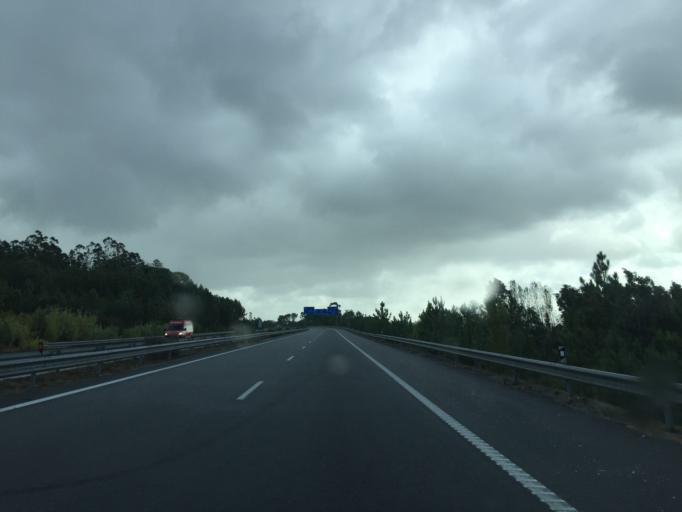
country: PT
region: Aveiro
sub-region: Mealhada
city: Pampilhosa do Botao
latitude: 40.2766
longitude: -8.5066
